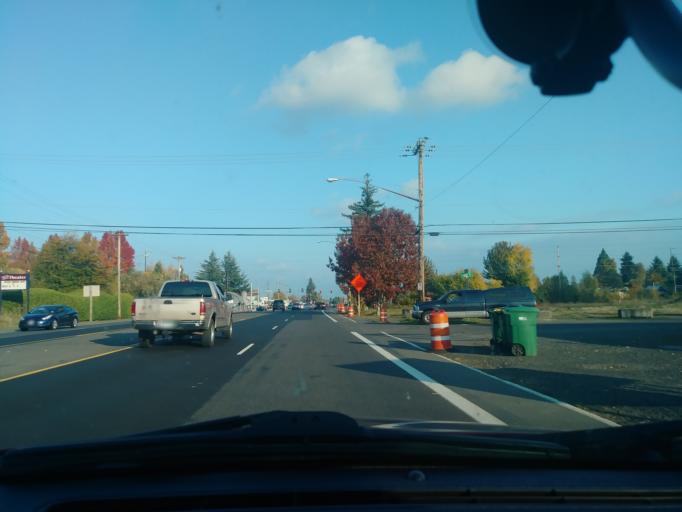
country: US
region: Oregon
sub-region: Washington County
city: Forest Grove
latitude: 45.5201
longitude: -123.0867
